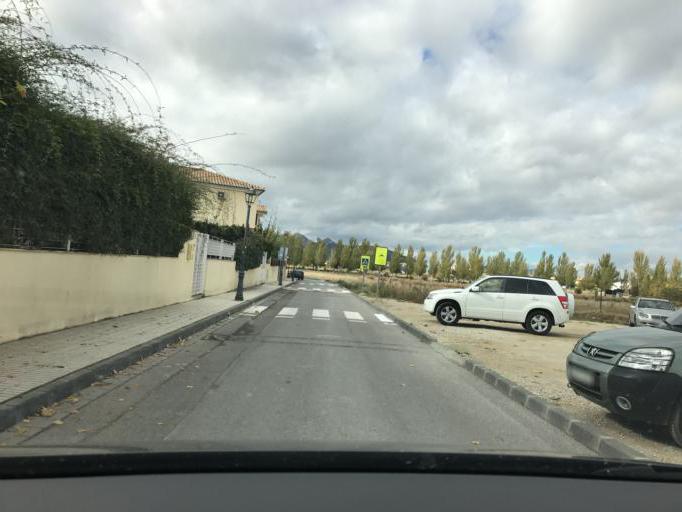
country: ES
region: Andalusia
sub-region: Provincia de Granada
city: Peligros
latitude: 37.2298
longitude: -3.6330
